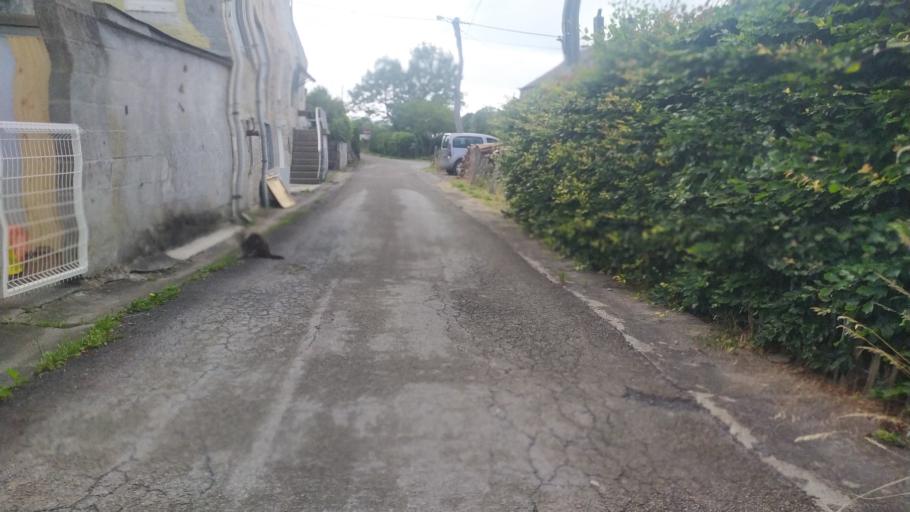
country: BE
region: Wallonia
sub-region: Province du Luxembourg
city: Wellin
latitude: 50.0810
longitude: 5.1079
